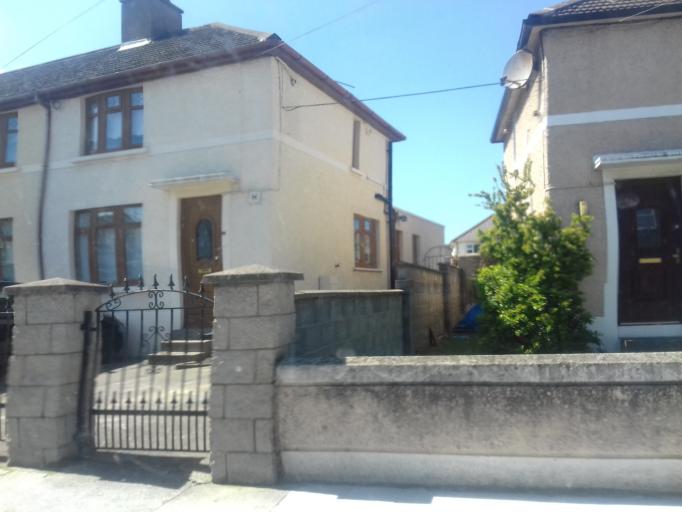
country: IE
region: Leinster
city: Cabra
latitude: 53.3684
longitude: -6.2900
